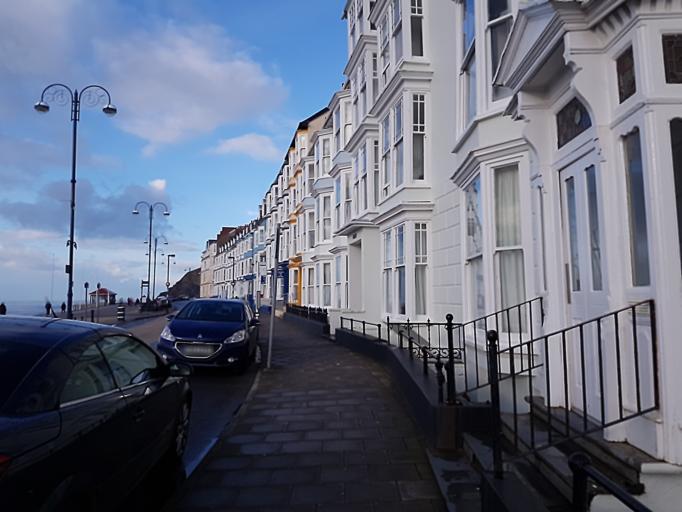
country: GB
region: Wales
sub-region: County of Ceredigion
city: Aberystwyth
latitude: 52.4178
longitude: -4.0840
